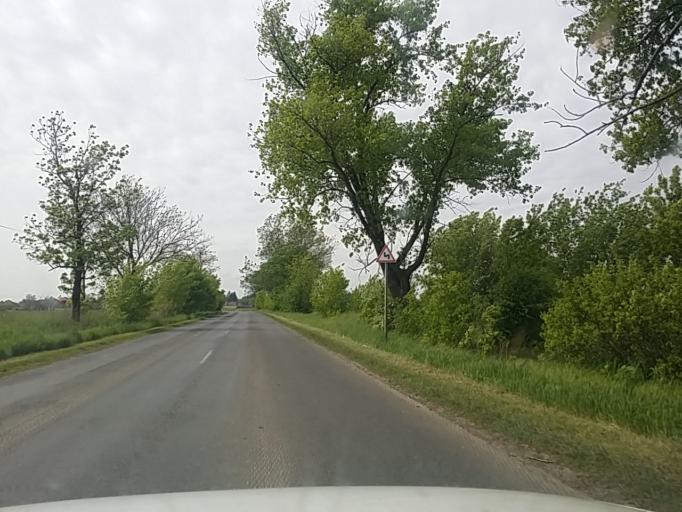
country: HU
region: Pest
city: Szentmartonkata
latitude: 47.4617
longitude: 19.7075
